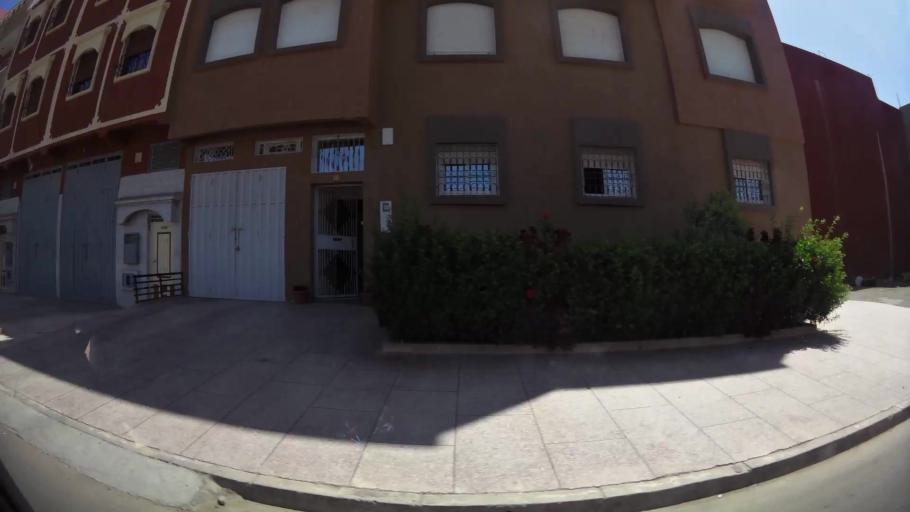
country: MA
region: Souss-Massa-Draa
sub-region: Inezgane-Ait Mellou
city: Inezgane
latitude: 30.3255
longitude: -9.5000
